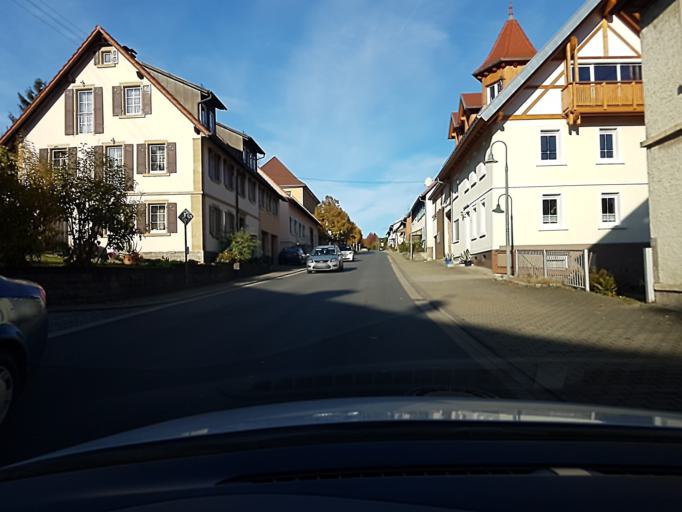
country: DE
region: Baden-Wuerttemberg
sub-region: Karlsruhe Region
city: Billigheim
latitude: 49.3475
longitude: 9.2528
